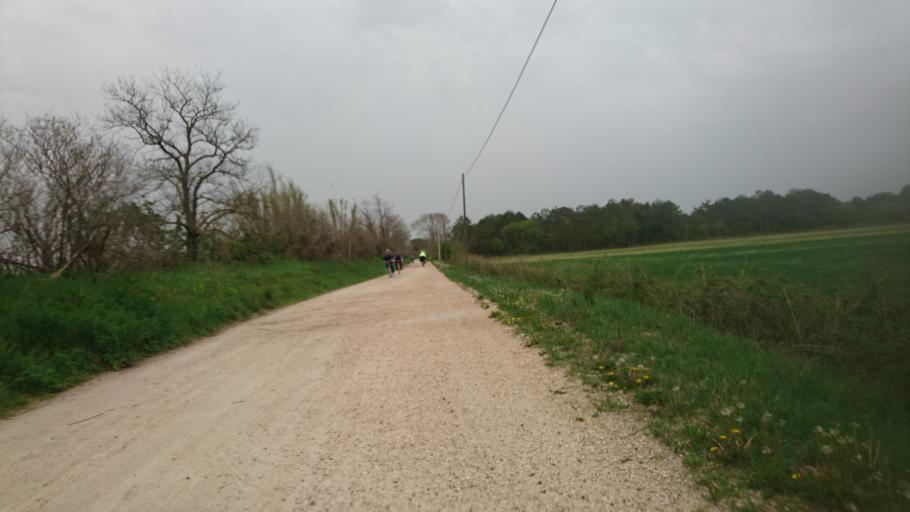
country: IT
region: Friuli Venezia Giulia
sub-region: Provincia di Udine
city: Lignano Sabbiadoro
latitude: 45.6484
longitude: 13.0826
